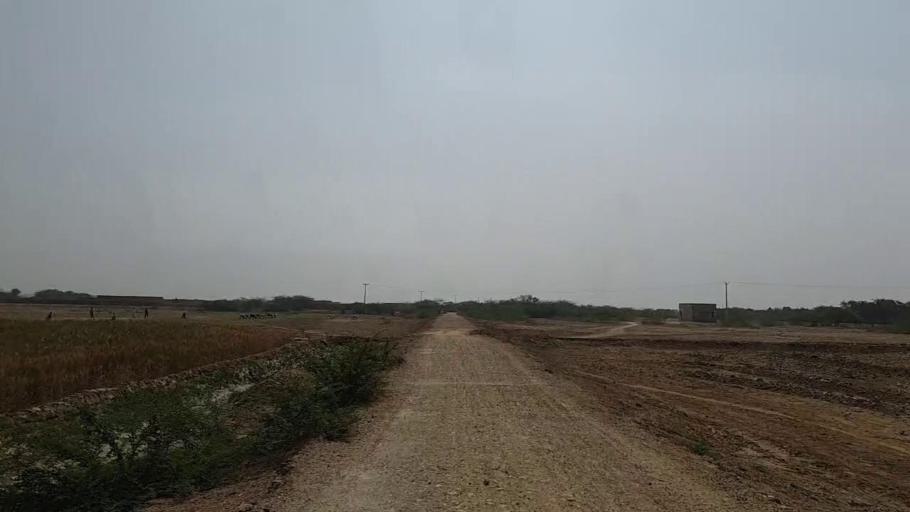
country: PK
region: Sindh
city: Naukot
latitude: 24.8145
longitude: 69.3595
